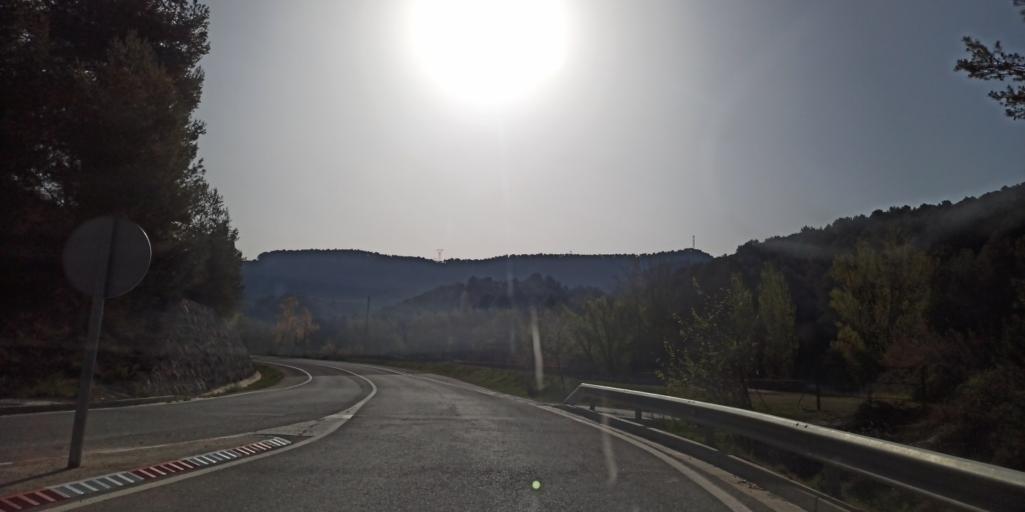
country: ES
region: Catalonia
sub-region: Provincia de Barcelona
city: Castelloli
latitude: 41.5868
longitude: 1.6768
